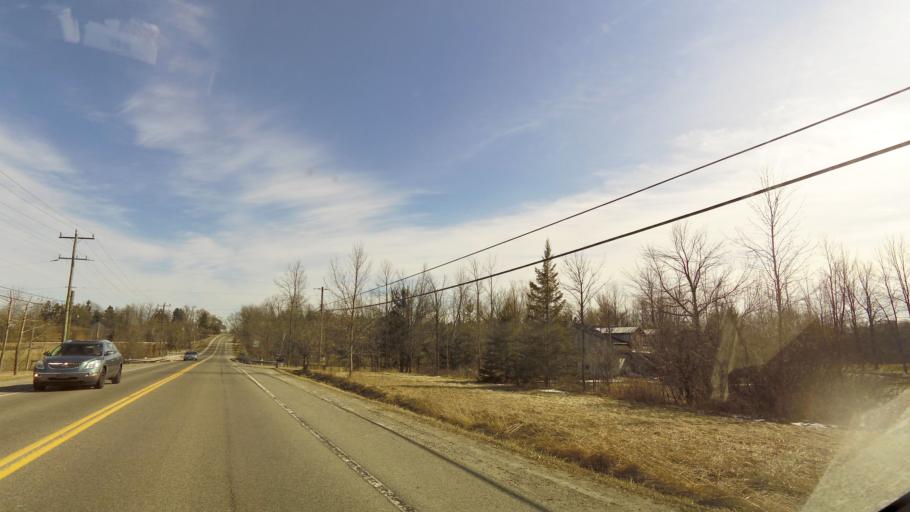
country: CA
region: Ontario
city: Burlington
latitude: 43.3526
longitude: -79.9244
